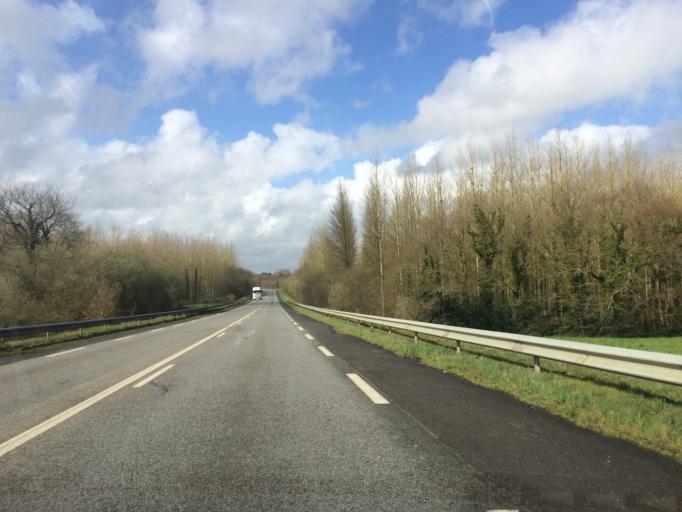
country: FR
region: Brittany
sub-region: Departement du Morbihan
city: La Gacilly
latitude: 47.7670
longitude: -2.1211
